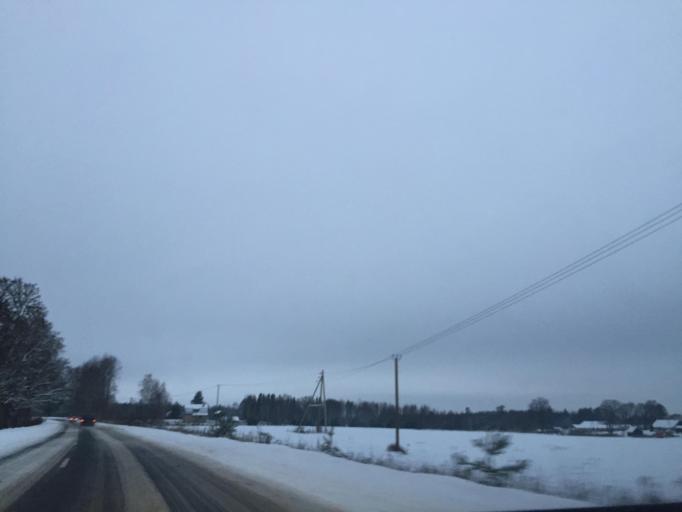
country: LV
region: Raunas
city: Rauna
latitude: 57.4353
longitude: 25.7085
